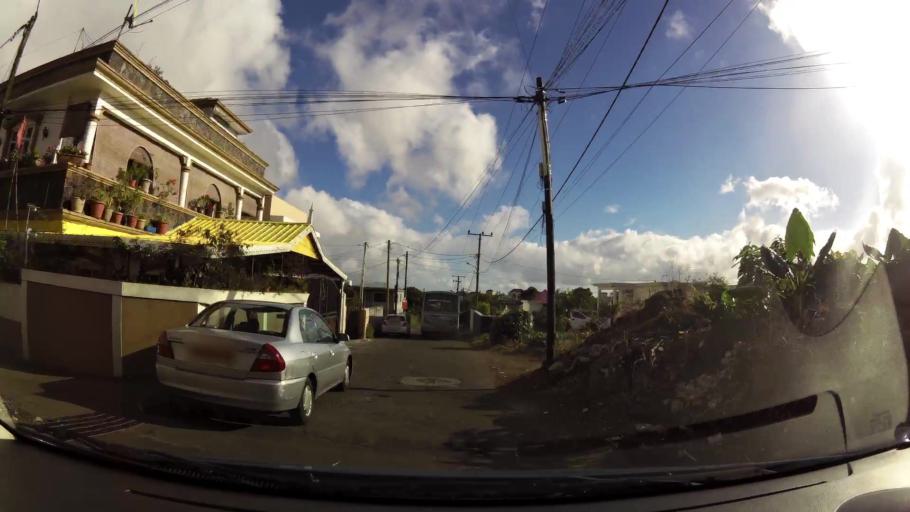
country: MU
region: Plaines Wilhems
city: Curepipe
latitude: -20.3250
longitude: 57.5071
